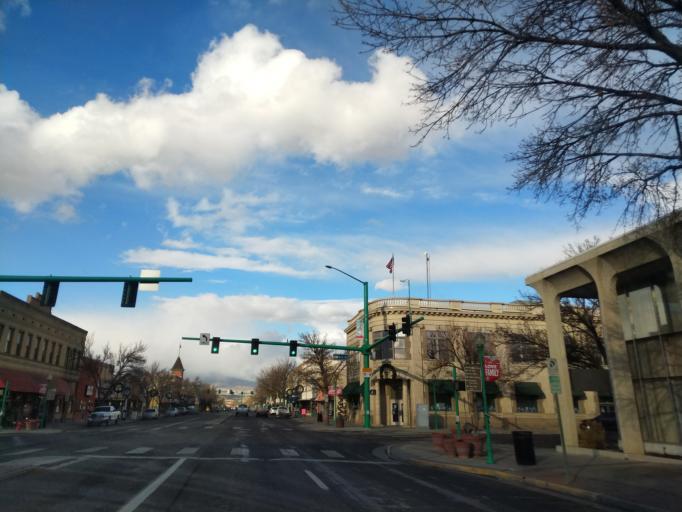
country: US
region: Colorado
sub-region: Delta County
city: Delta
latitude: 38.7414
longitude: -108.0708
